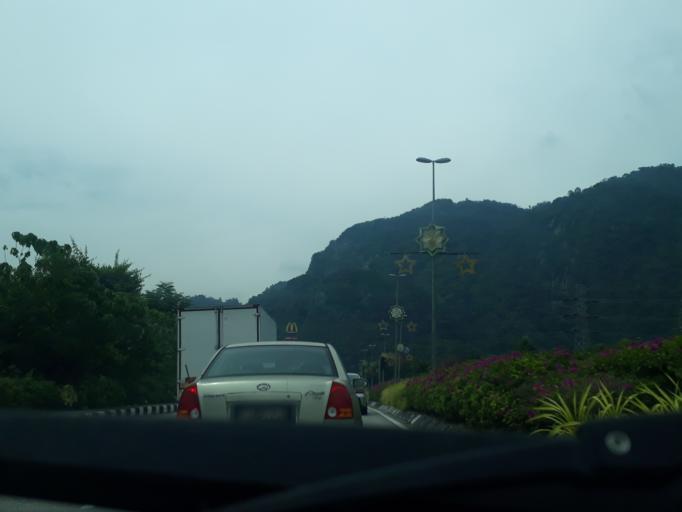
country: MY
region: Perak
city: Ipoh
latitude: 4.6231
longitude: 101.1500
